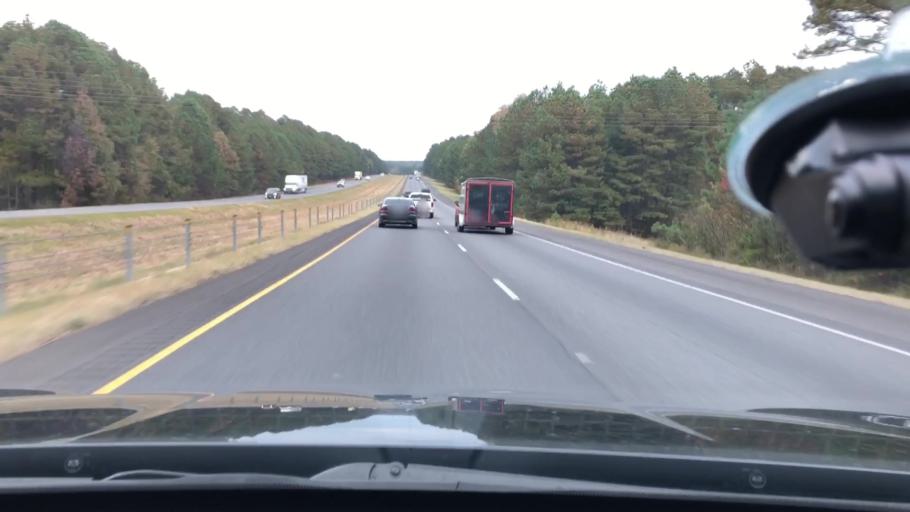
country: US
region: Arkansas
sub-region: Clark County
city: Arkadelphia
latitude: 34.2057
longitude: -93.0431
